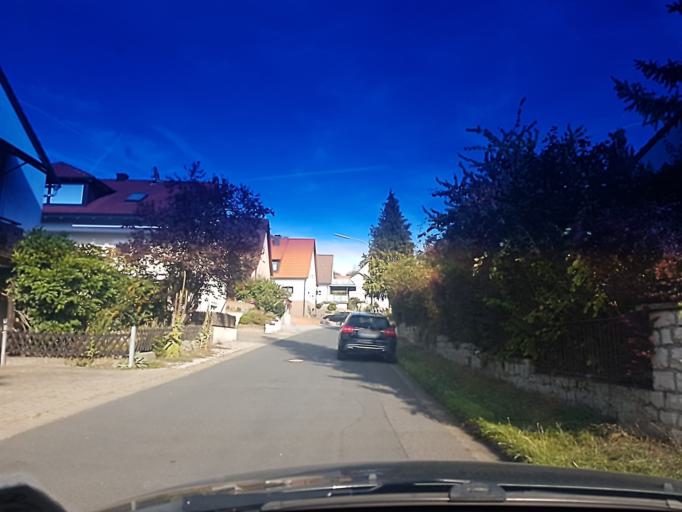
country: DE
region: Bavaria
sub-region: Regierungsbezirk Mittelfranken
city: Burghaslach
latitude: 49.7695
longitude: 10.5658
